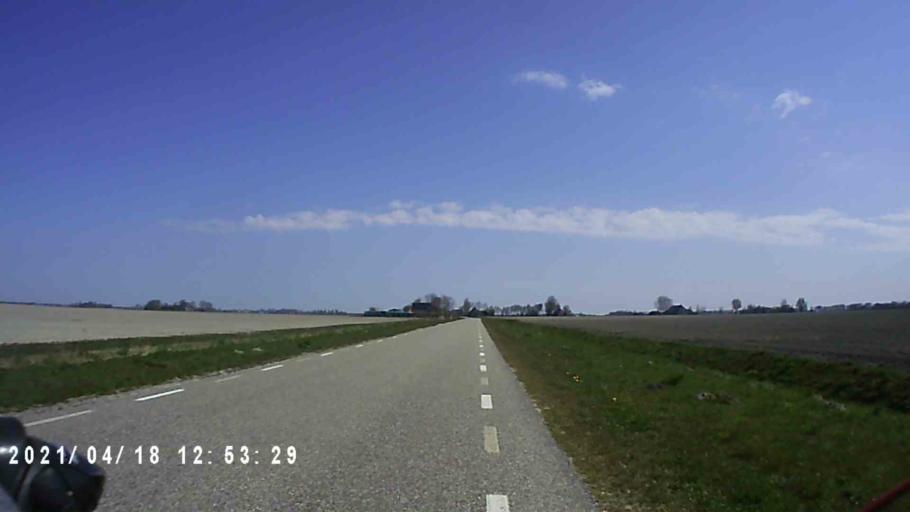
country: NL
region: Friesland
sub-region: Gemeente Dongeradeel
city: Anjum
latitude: 53.3834
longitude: 6.0663
